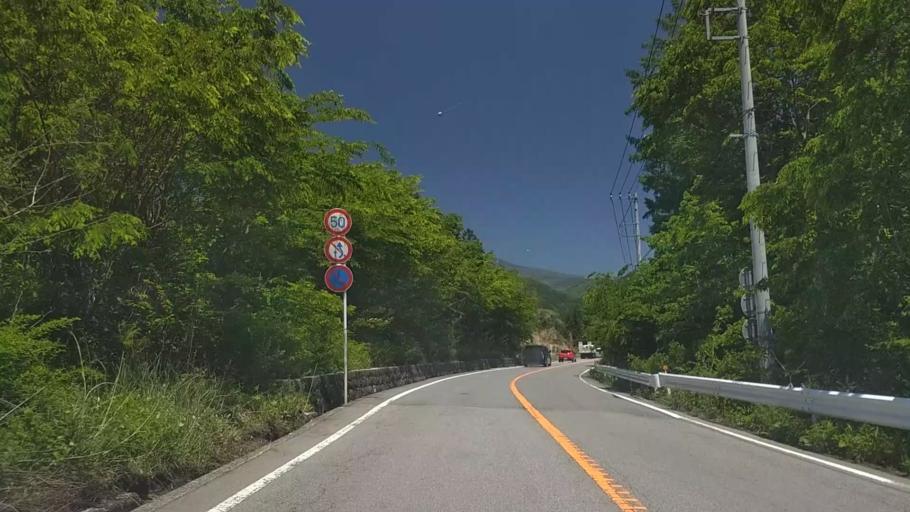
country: JP
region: Yamanashi
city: Nirasaki
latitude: 35.8578
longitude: 138.4303
